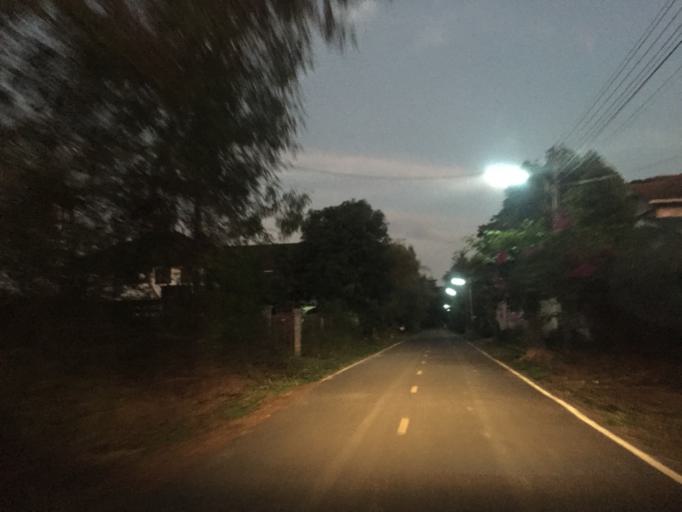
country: TH
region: Chiang Mai
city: Saraphi
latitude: 18.7267
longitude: 99.0307
